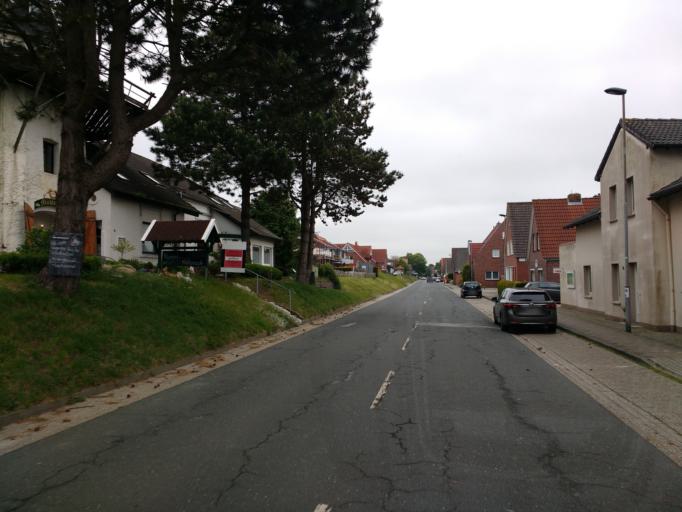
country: DE
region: Lower Saxony
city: Werdum
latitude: 53.6922
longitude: 7.7934
